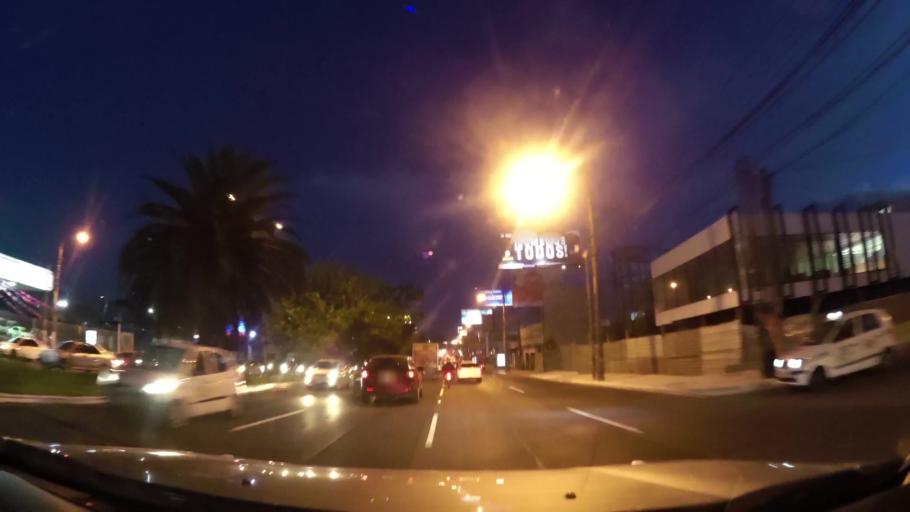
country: GT
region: Guatemala
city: Guatemala City
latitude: 14.6207
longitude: -90.5476
